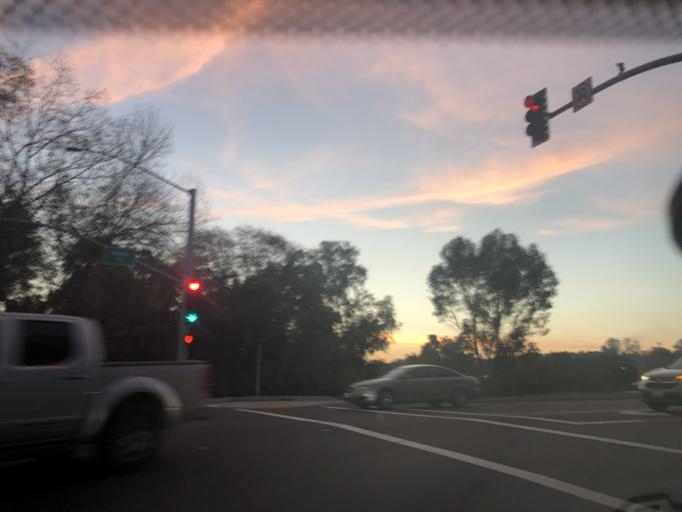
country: US
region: California
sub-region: San Diego County
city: Bonita
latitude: 32.6601
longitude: -117.0437
